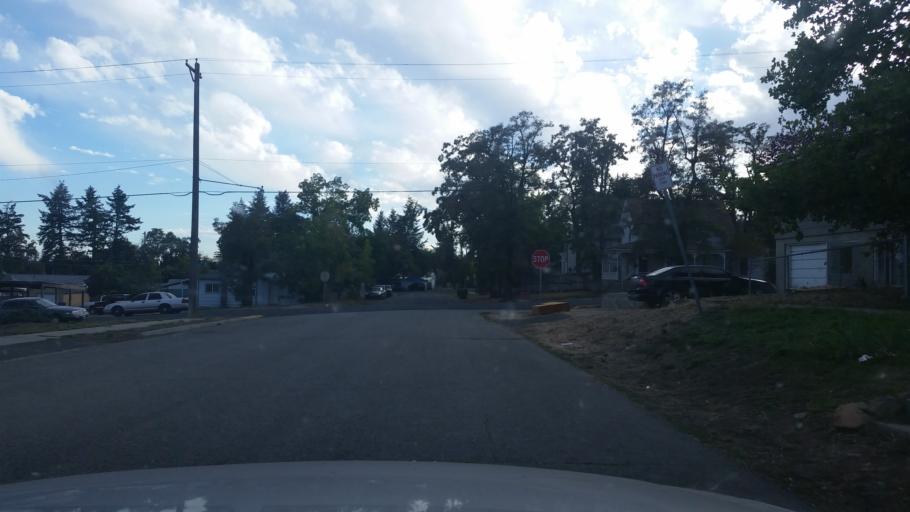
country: US
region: Washington
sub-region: Spokane County
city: Cheney
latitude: 47.4866
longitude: -117.5807
